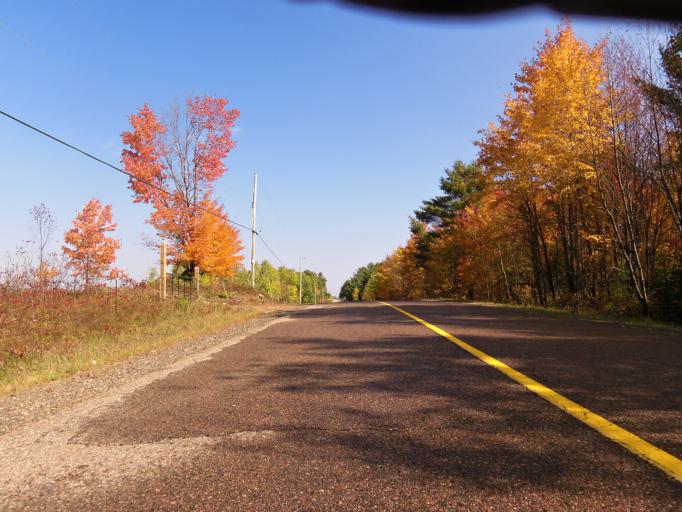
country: CA
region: Ontario
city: Petawawa
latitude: 45.8153
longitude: -77.2510
